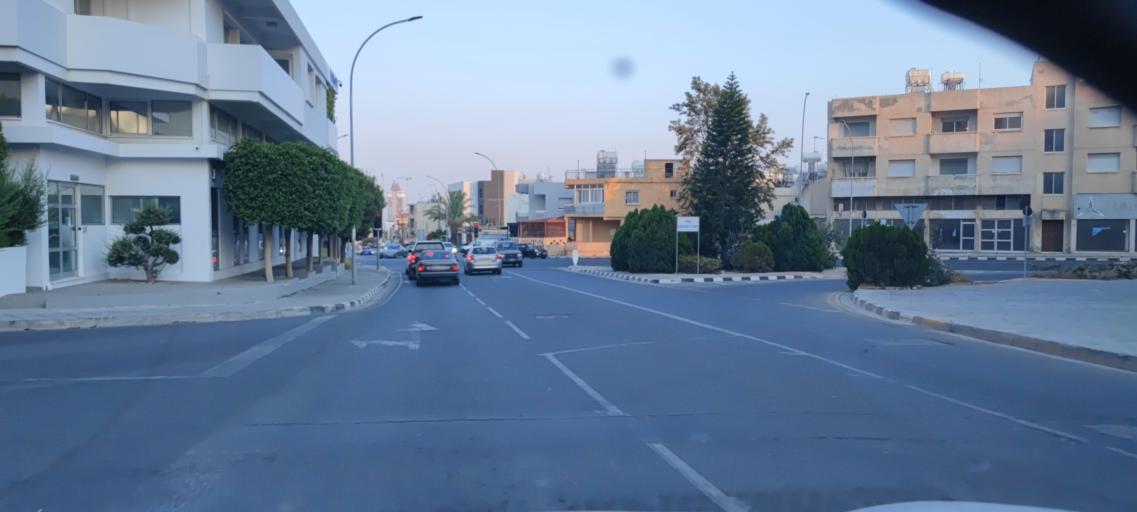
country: CY
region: Limassol
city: Limassol
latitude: 34.6988
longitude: 33.0473
